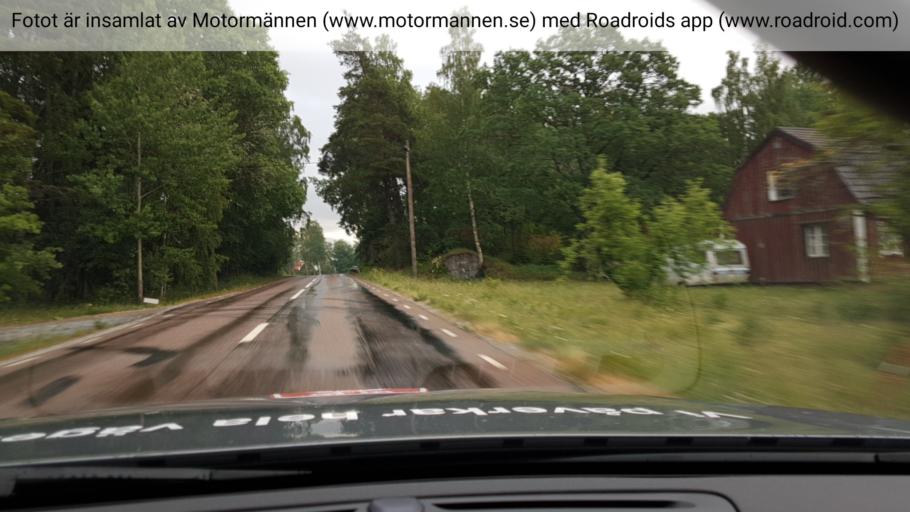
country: SE
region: Vaestmanland
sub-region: Surahammars Kommun
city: Ramnas
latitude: 59.9497
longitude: 16.2578
